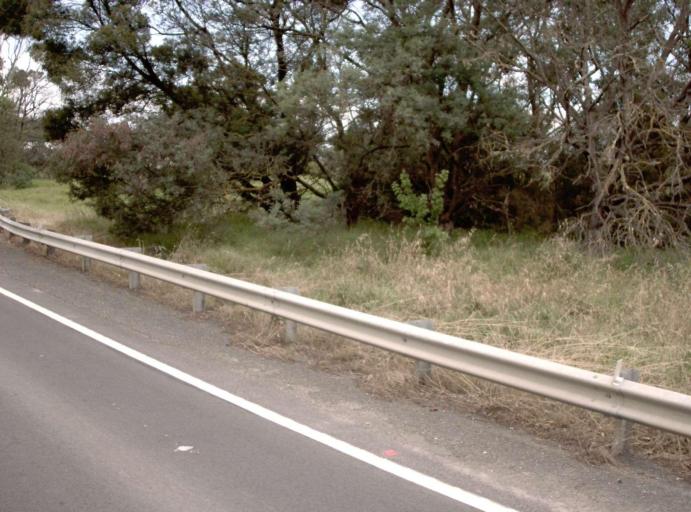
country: AU
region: Victoria
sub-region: Wellington
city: Sale
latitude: -37.9794
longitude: 147.0726
